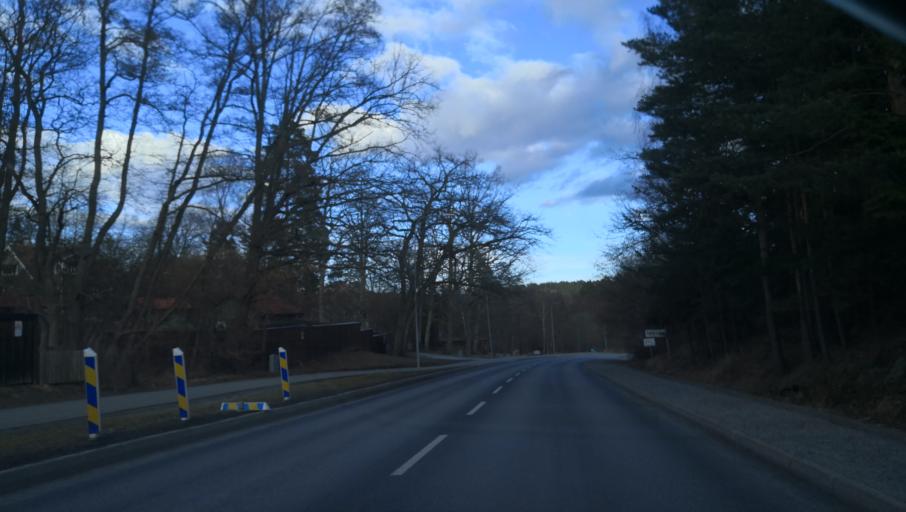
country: SE
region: Stockholm
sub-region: Nacka Kommun
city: Boo
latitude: 59.3335
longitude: 18.3267
